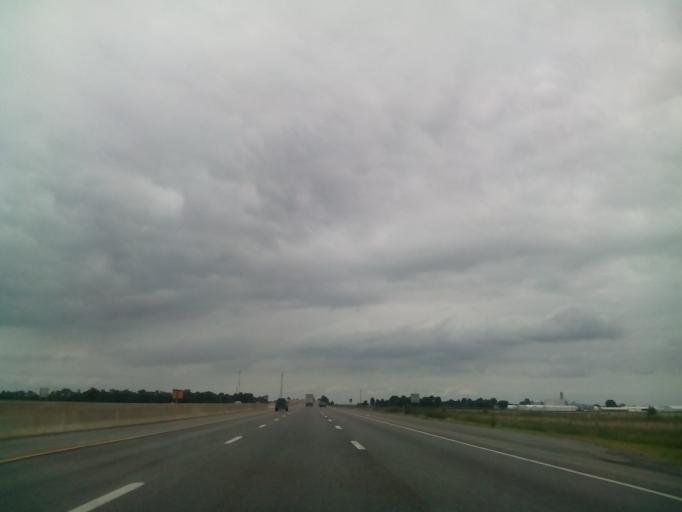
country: US
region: Ohio
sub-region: Huron County
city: Monroeville
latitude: 41.3359
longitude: -82.7118
